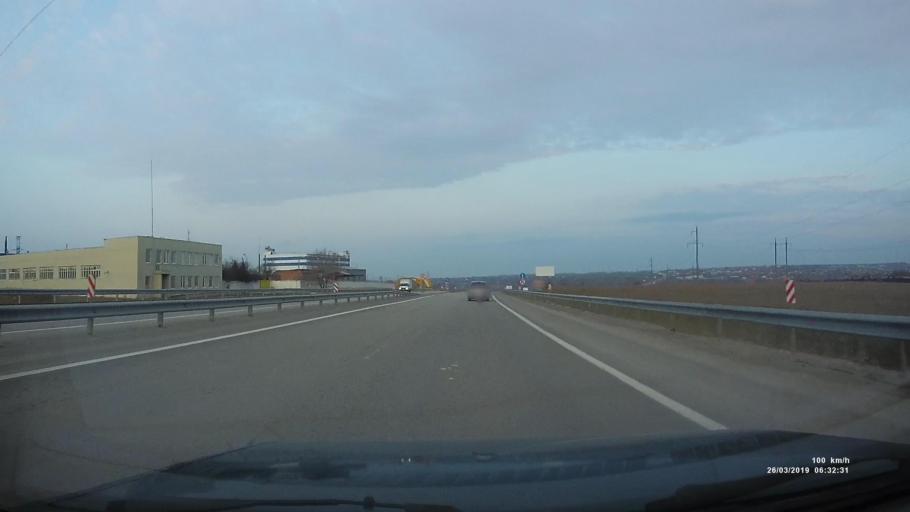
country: RU
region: Rostov
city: Kalinin
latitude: 47.2702
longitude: 39.5084
